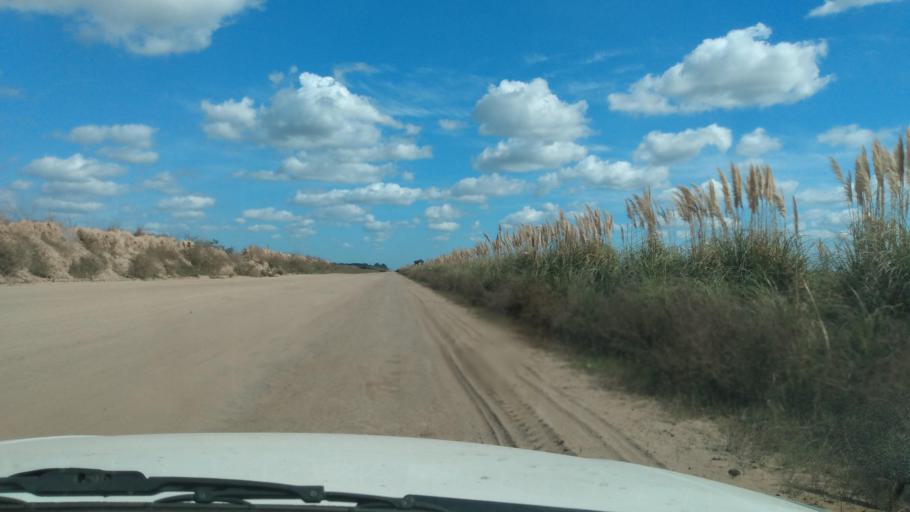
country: AR
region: Buenos Aires
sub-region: Partido de Navarro
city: Navarro
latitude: -35.0033
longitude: -59.3639
